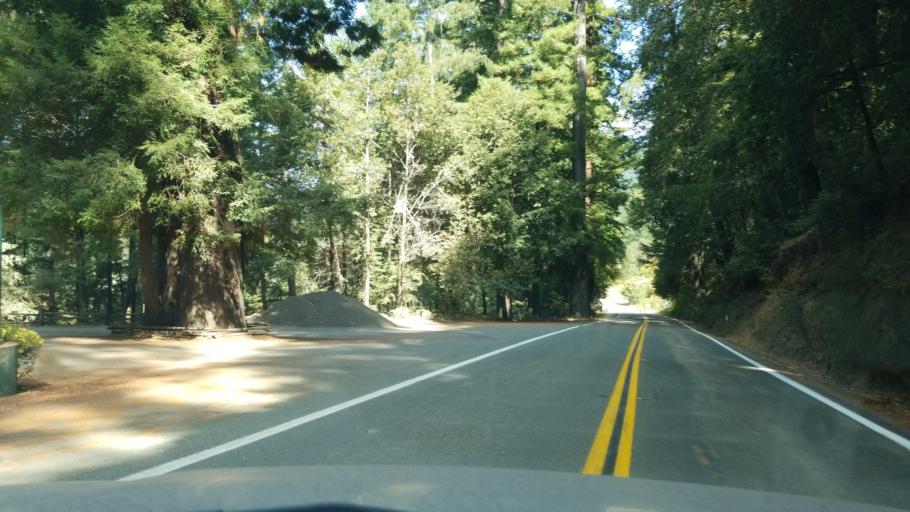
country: US
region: California
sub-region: Humboldt County
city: Redway
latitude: 39.8603
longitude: -123.7161
